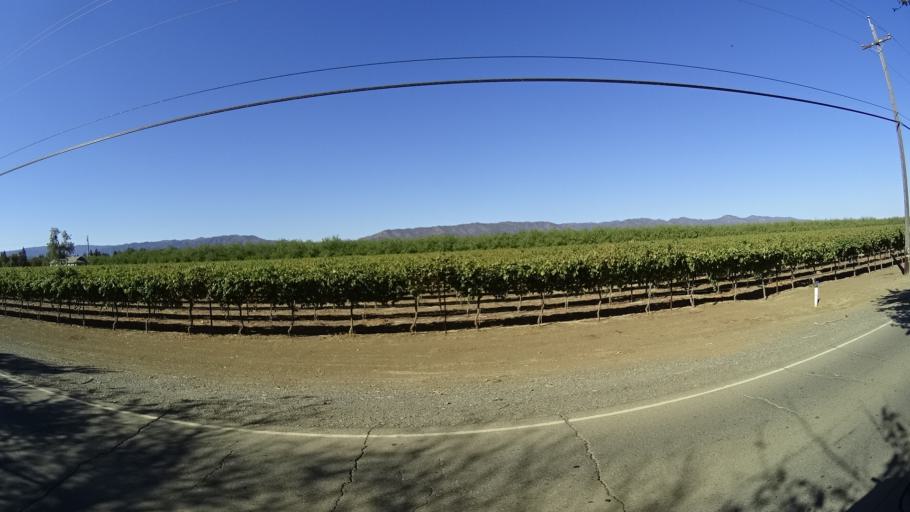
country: US
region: California
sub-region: Yolo County
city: Winters
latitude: 38.5347
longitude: -121.9710
